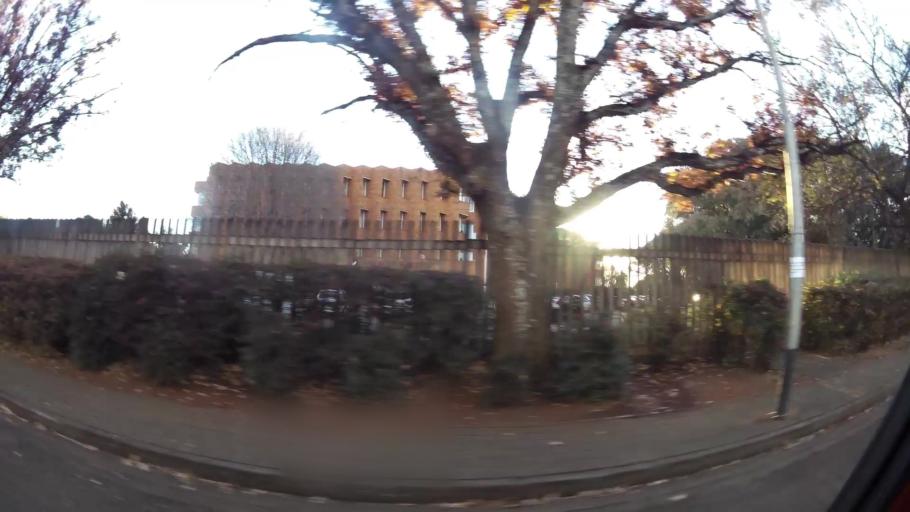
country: ZA
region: North-West
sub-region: Dr Kenneth Kaunda District Municipality
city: Potchefstroom
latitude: -26.6837
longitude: 27.0955
